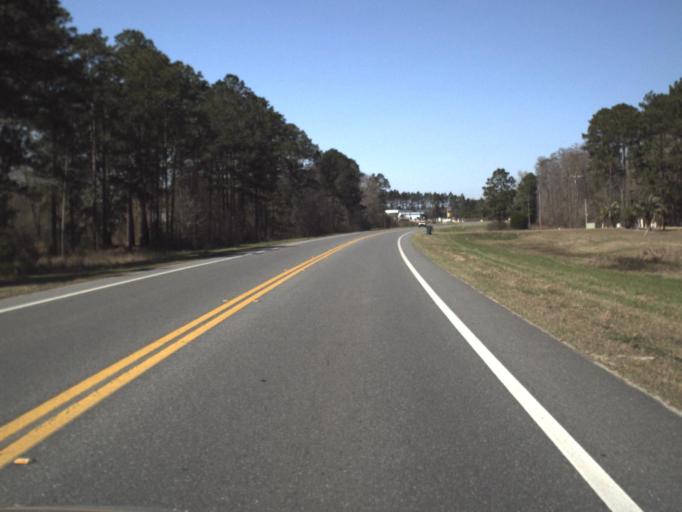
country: US
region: Florida
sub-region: Jackson County
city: Sneads
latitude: 30.7206
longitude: -85.0742
